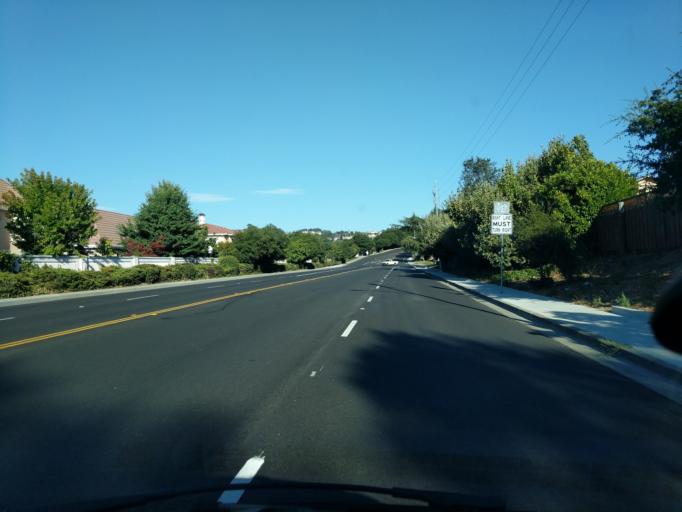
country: US
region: California
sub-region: Alameda County
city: Fairview
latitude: 37.6554
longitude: -122.0358
